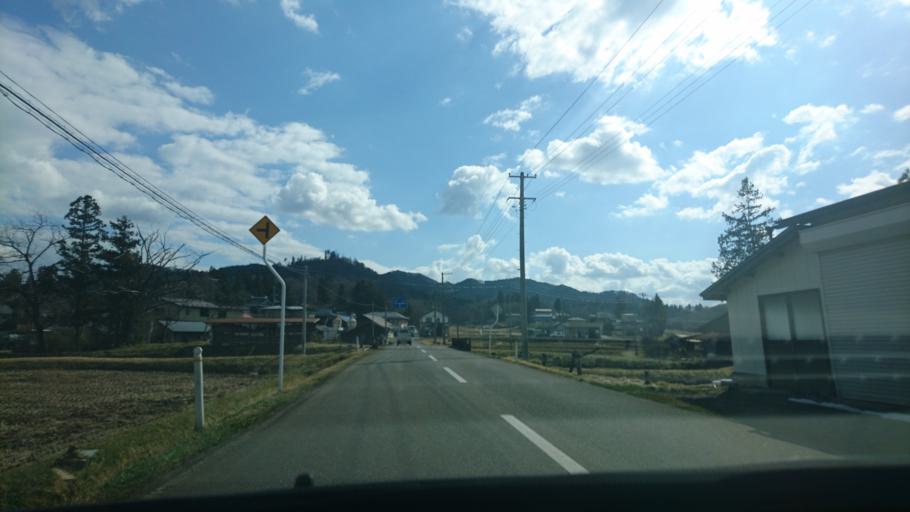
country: JP
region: Iwate
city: Kitakami
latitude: 39.2984
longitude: 141.2022
